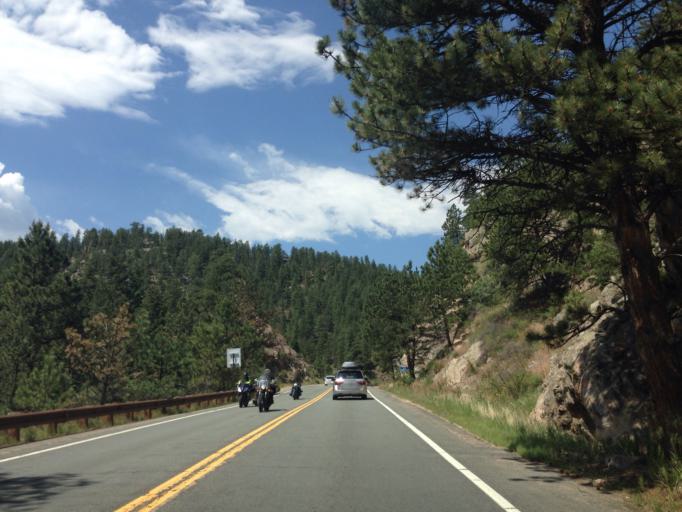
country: US
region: Colorado
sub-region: Larimer County
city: Estes Park
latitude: 40.4084
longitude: -105.4061
